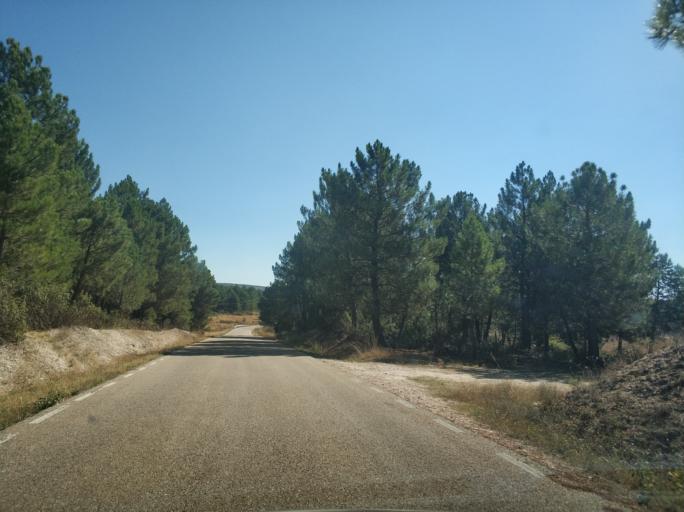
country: ES
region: Castille and Leon
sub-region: Provincia de Soria
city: Santa Maria de las Hoyas
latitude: 41.7762
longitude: -3.1812
